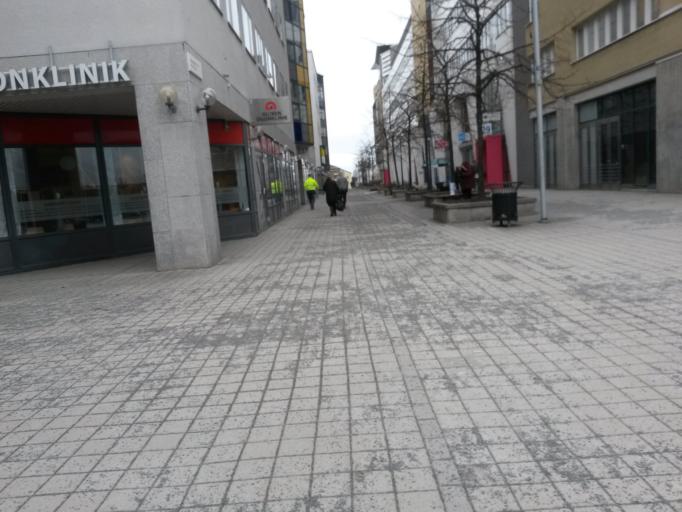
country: SE
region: Stockholm
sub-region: Stockholms Kommun
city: Arsta
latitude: 59.2954
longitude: 18.0807
